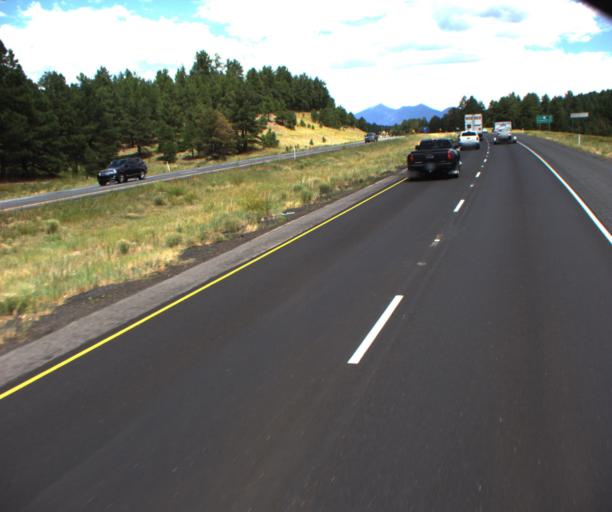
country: US
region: Arizona
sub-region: Coconino County
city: Kachina Village
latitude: 35.1029
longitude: -111.6815
